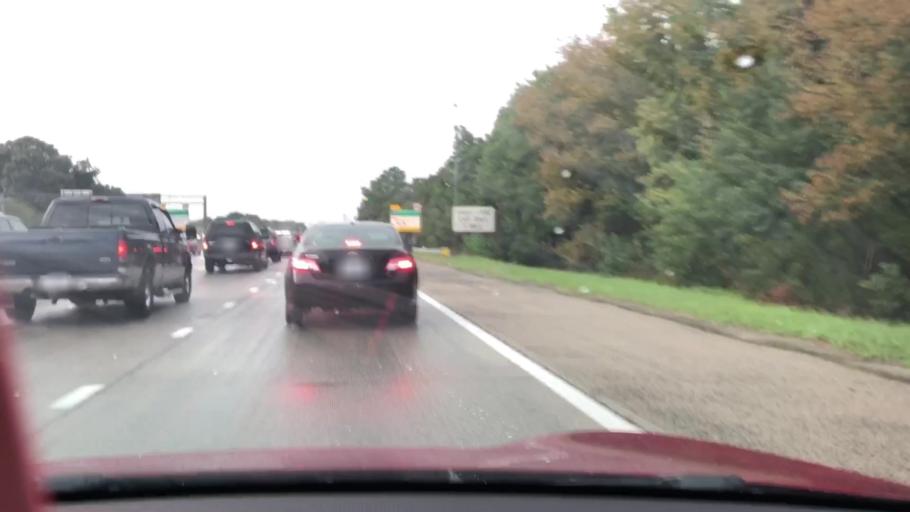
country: US
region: Virginia
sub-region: City of Chesapeake
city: Chesapeake
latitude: 36.8245
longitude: -76.1949
